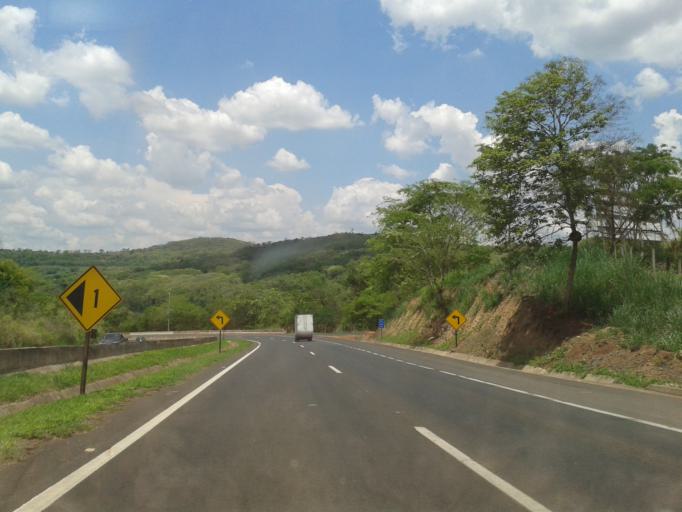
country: BR
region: Minas Gerais
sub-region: Araguari
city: Araguari
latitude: -18.7685
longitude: -48.2454
